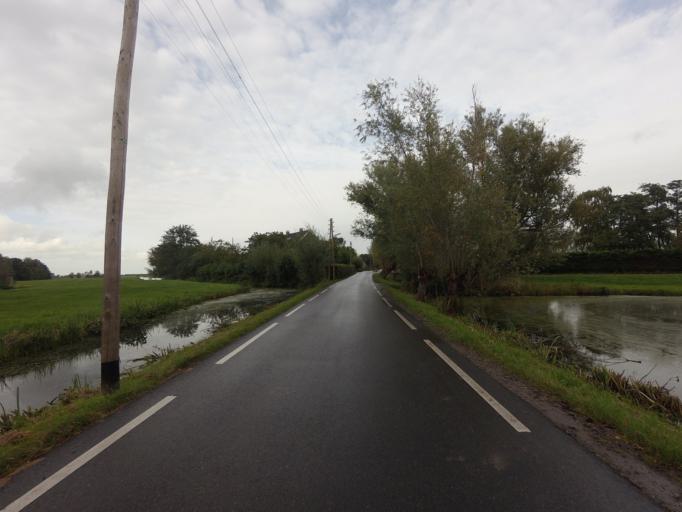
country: NL
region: South Holland
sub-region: Molenwaard
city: Liesveld
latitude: 51.9500
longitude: 4.8177
